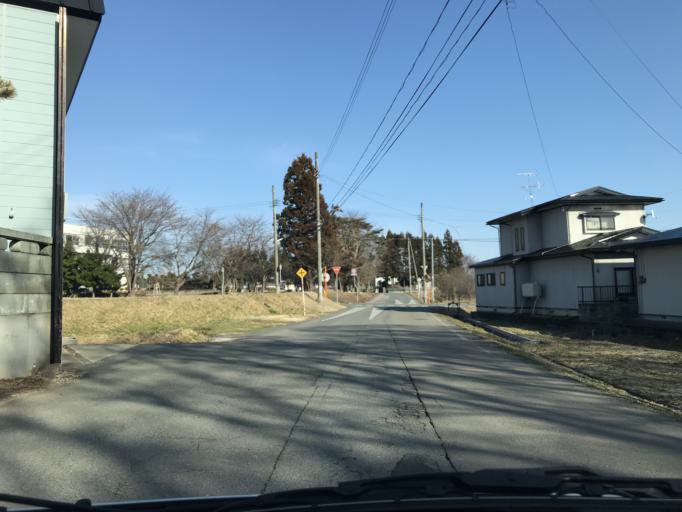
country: JP
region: Iwate
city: Kitakami
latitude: 39.2966
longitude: 141.0273
